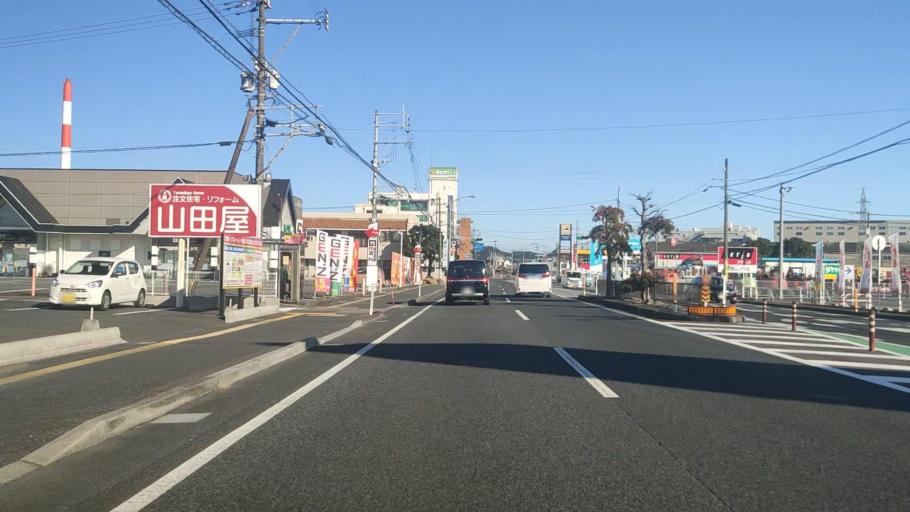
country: JP
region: Miyazaki
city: Nobeoka
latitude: 32.5939
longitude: 131.6766
